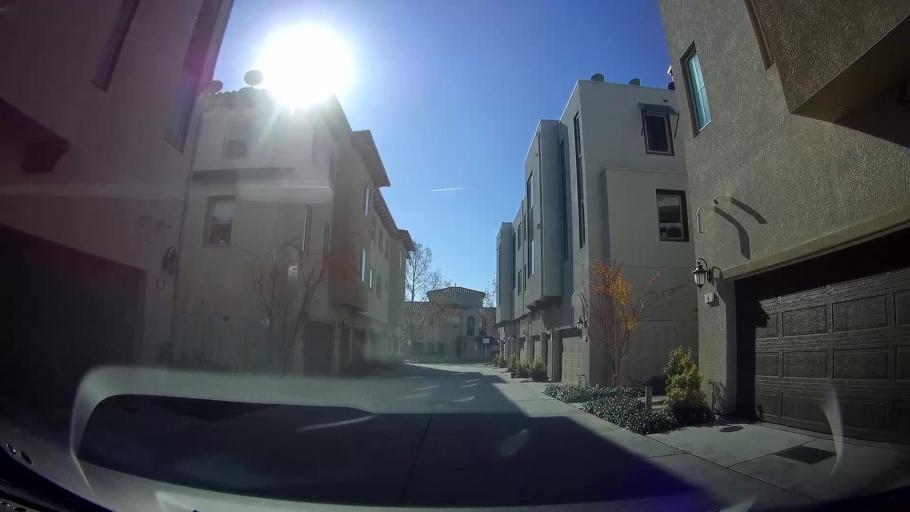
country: US
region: California
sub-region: Santa Clara County
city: Seven Trees
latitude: 37.2846
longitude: -121.8567
